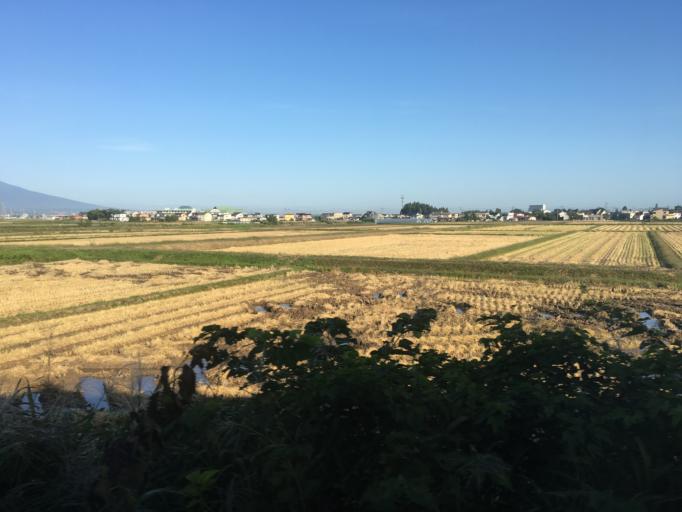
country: JP
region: Aomori
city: Kuroishi
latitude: 40.5812
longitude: 140.5589
